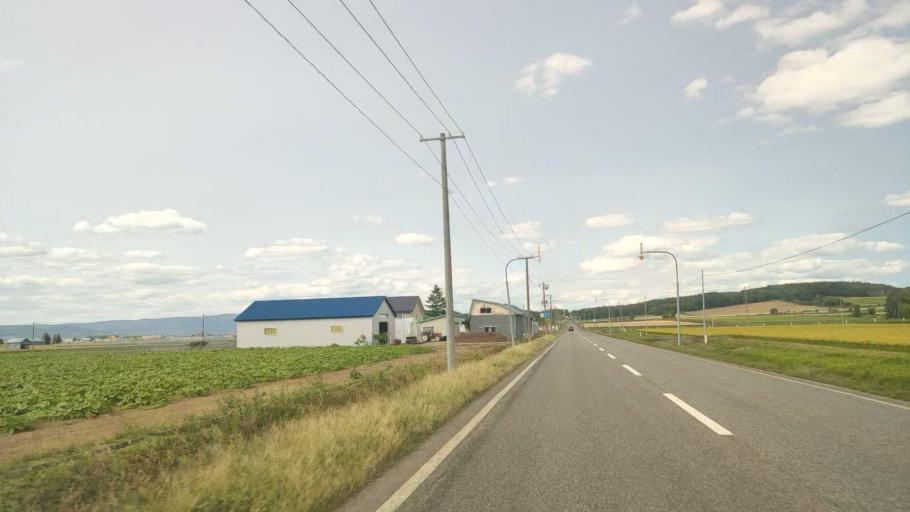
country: JP
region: Hokkaido
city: Nayoro
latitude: 44.2295
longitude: 142.4157
